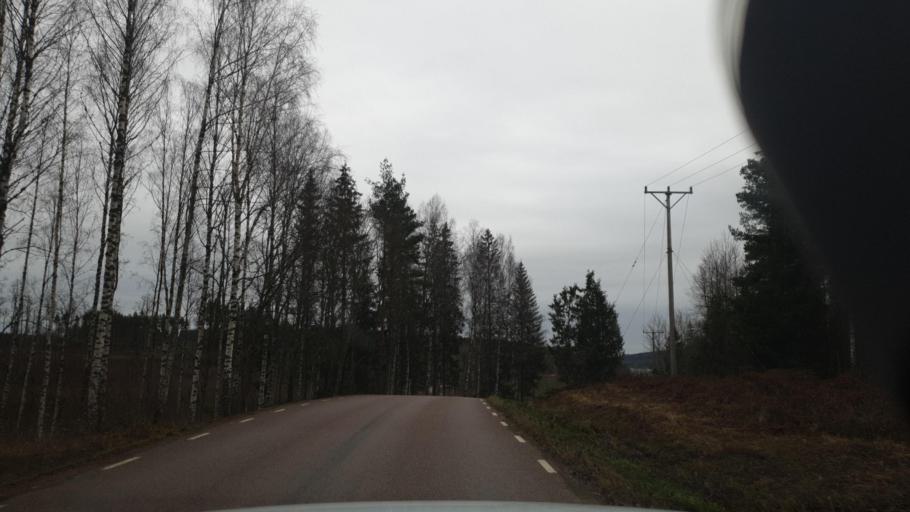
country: SE
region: Vaermland
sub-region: Karlstads Kommun
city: Valberg
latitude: 59.4439
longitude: 13.0909
